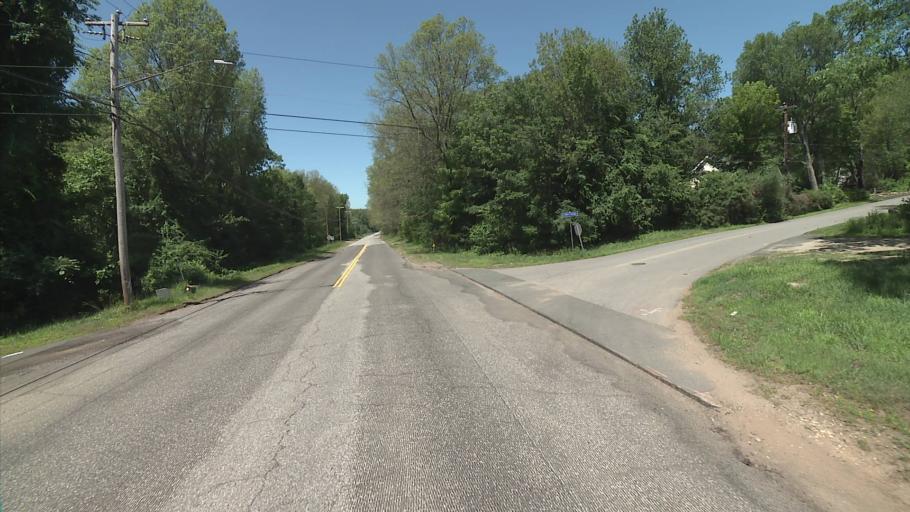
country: US
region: Connecticut
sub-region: Middlesex County
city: East Hampton
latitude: 41.5642
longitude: -72.5292
